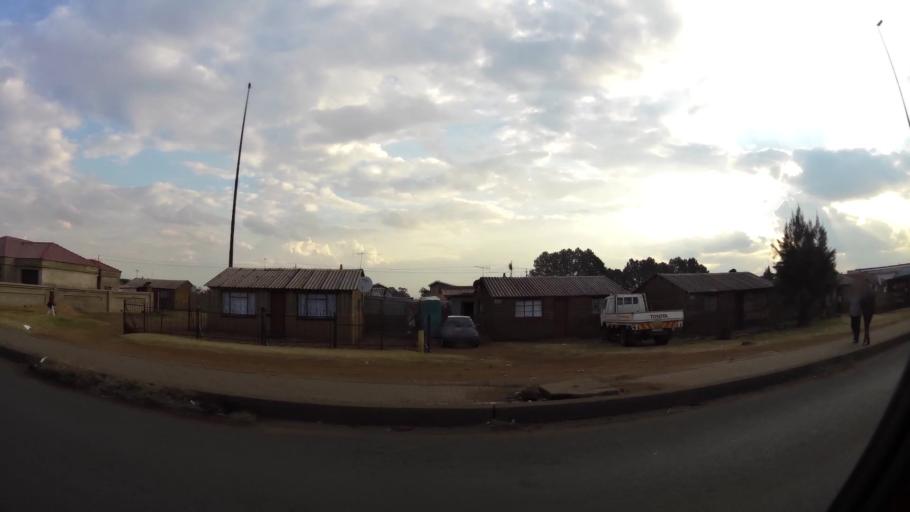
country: ZA
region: Gauteng
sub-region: City of Johannesburg Metropolitan Municipality
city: Orange Farm
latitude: -26.5752
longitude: 27.8398
